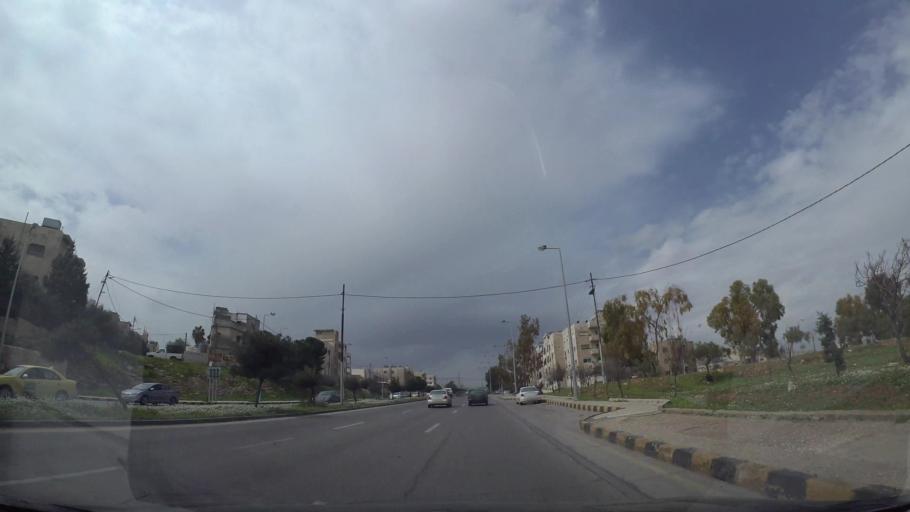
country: JO
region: Amman
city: Amman
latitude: 31.9741
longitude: 35.9339
